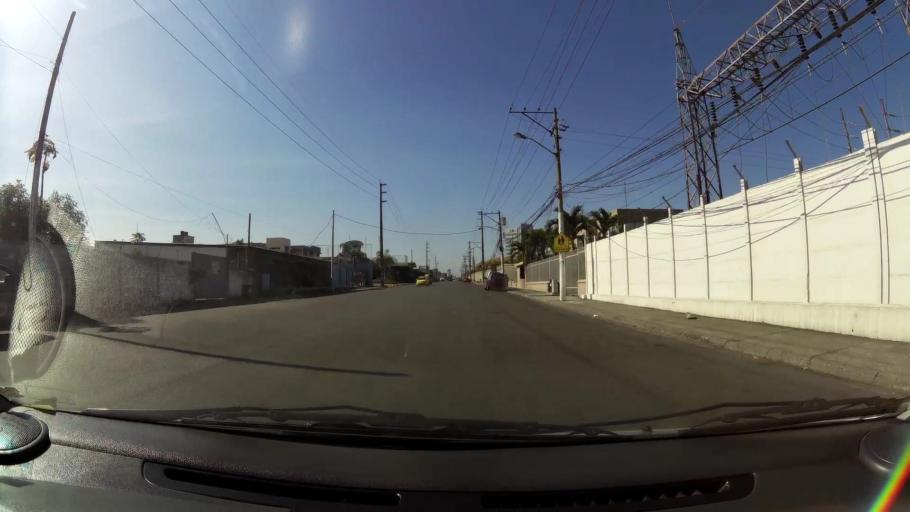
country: EC
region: Guayas
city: Eloy Alfaro
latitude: -2.1545
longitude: -79.8993
